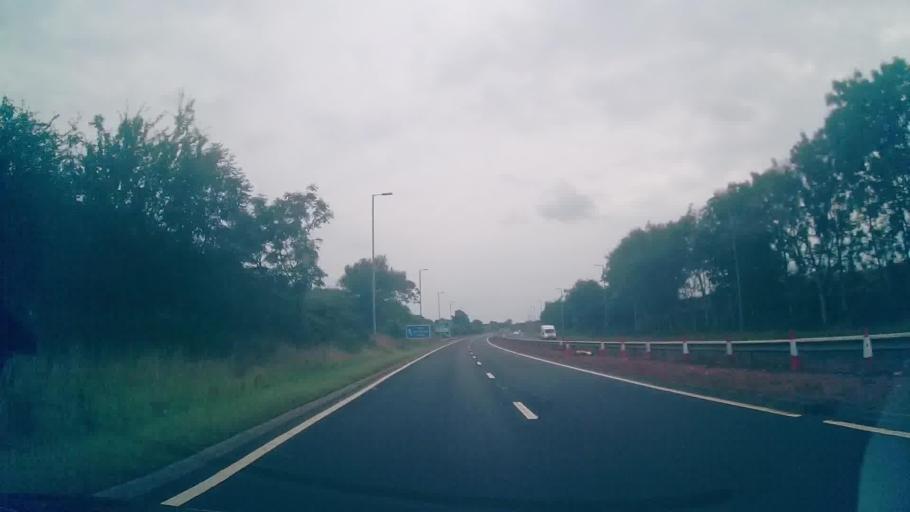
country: GB
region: Scotland
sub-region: Dumfries and Galloway
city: Gretna
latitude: 54.9995
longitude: -3.0751
